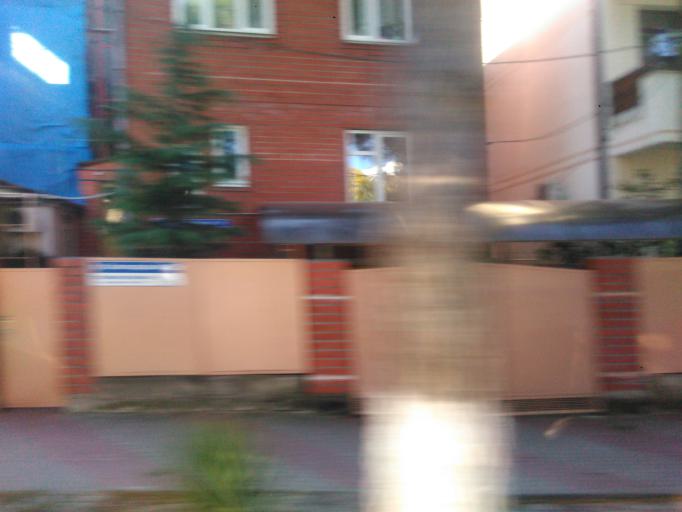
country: RU
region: Krasnodarskiy
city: Gelendzhik
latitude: 44.5530
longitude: 38.0695
